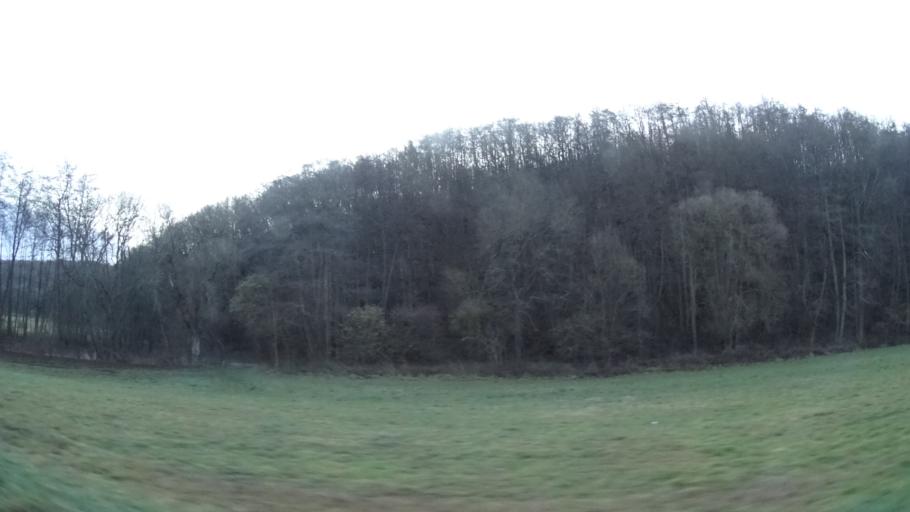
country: DE
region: Rheinland-Pfalz
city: Wendelsheim
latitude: 49.7546
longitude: 7.9851
